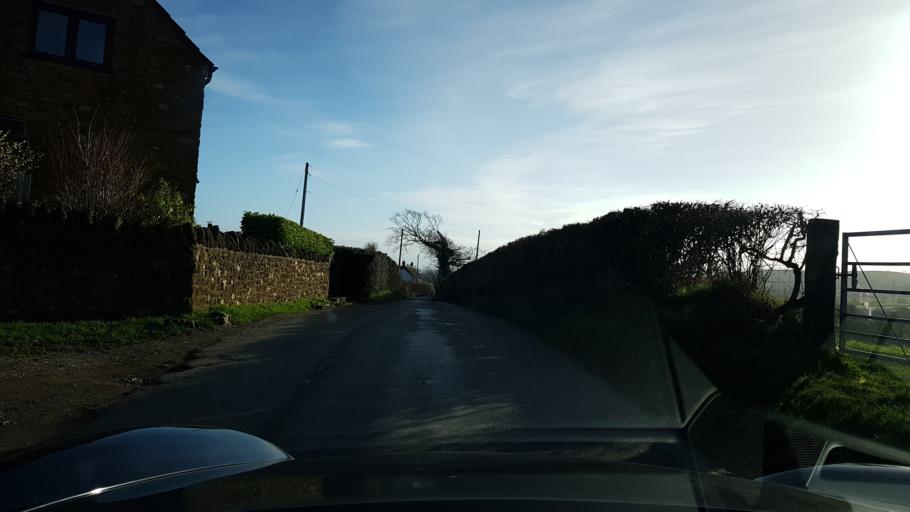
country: GB
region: England
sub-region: Dorset
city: Bridport
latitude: 50.7807
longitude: -2.8339
